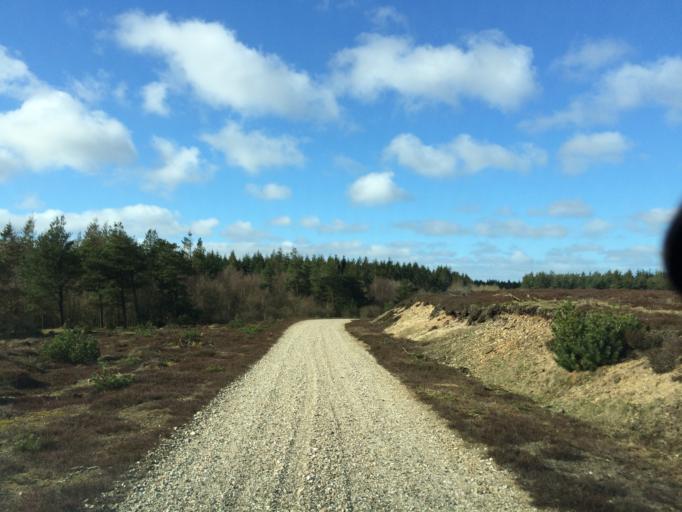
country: DK
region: Central Jutland
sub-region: Holstebro Kommune
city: Ulfborg
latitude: 56.2851
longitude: 8.4261
